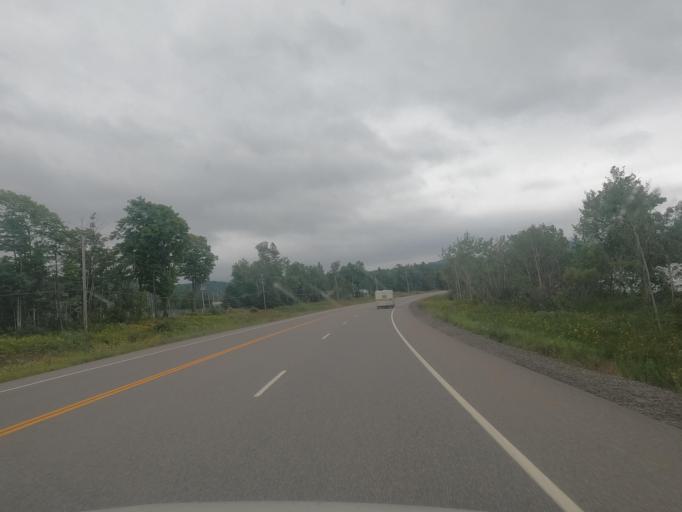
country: CA
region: Ontario
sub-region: Algoma
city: Sault Ste. Marie
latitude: 46.8926
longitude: -84.3639
